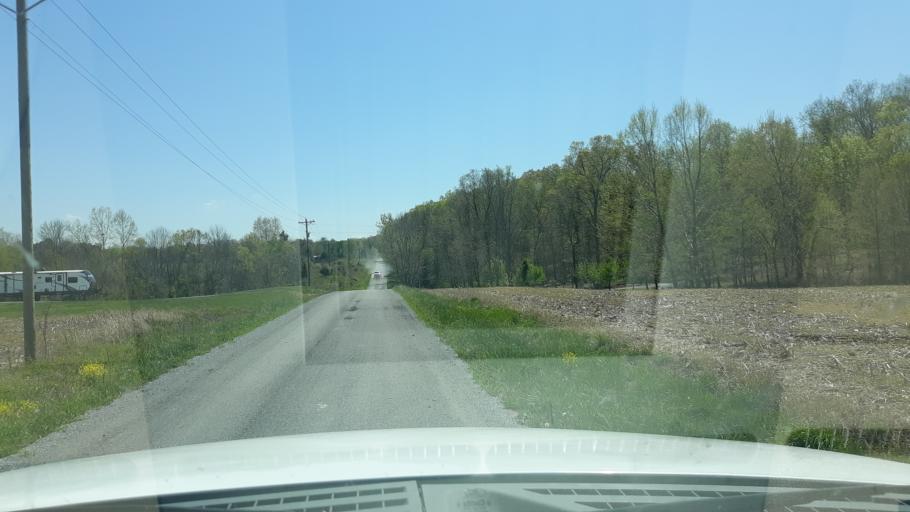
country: US
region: Illinois
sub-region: Saline County
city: Harrisburg
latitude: 37.8754
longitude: -88.6421
